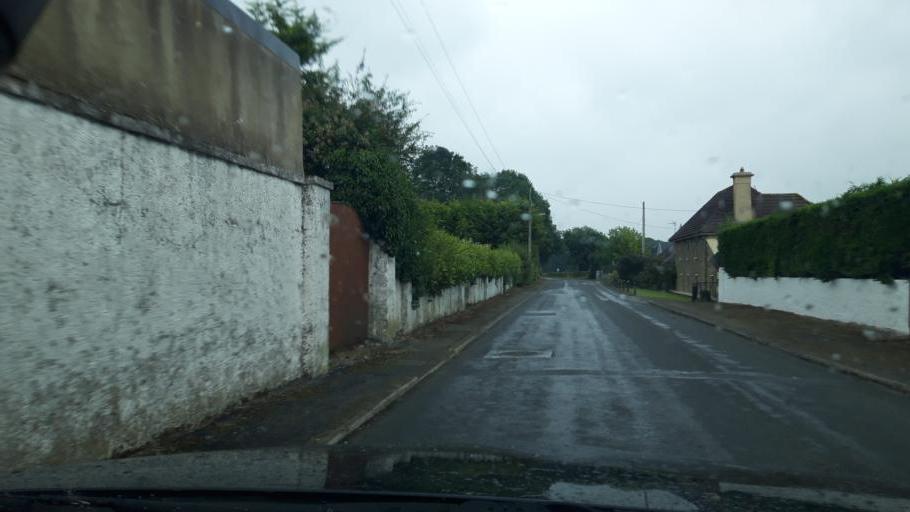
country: IE
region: Leinster
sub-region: Kilkenny
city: Callan
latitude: 52.6618
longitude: -7.4380
